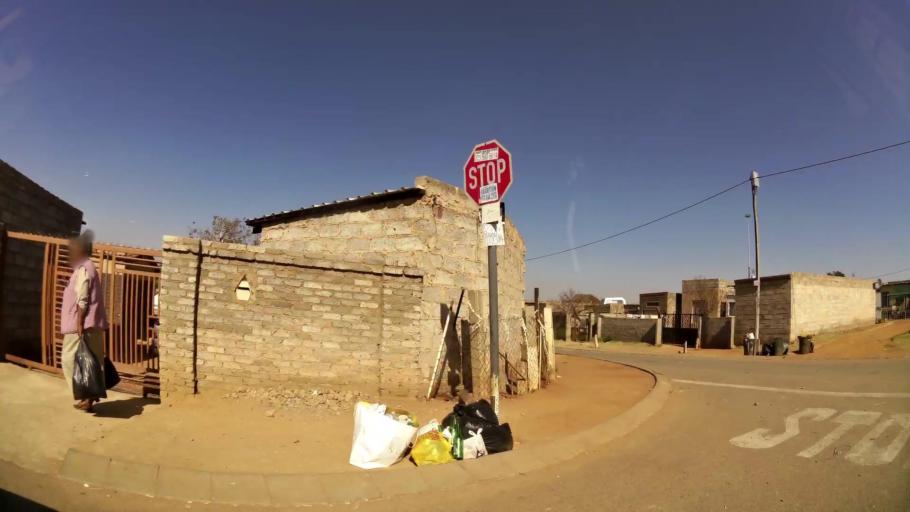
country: ZA
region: Gauteng
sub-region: Ekurhuleni Metropolitan Municipality
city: Tembisa
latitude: -26.0263
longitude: 28.2389
